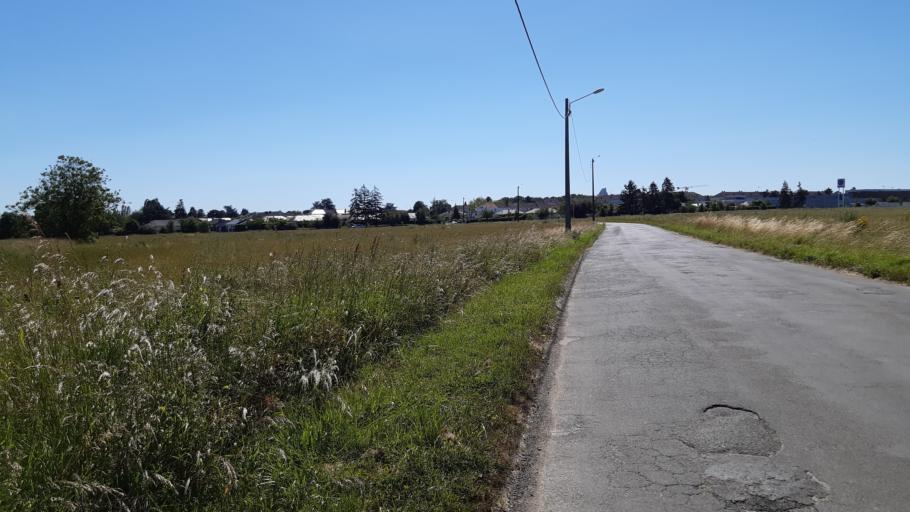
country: FR
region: Centre
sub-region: Departement d'Indre-et-Loire
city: Saint-Cyr-sur-Loire
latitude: 47.4292
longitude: 0.6693
